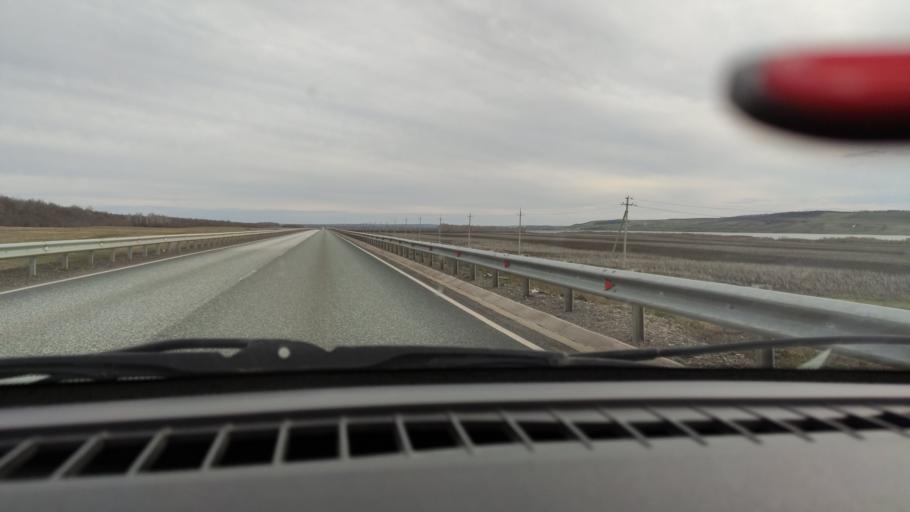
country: RU
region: Bashkortostan
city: Yermolayevo
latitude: 52.5271
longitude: 55.8326
